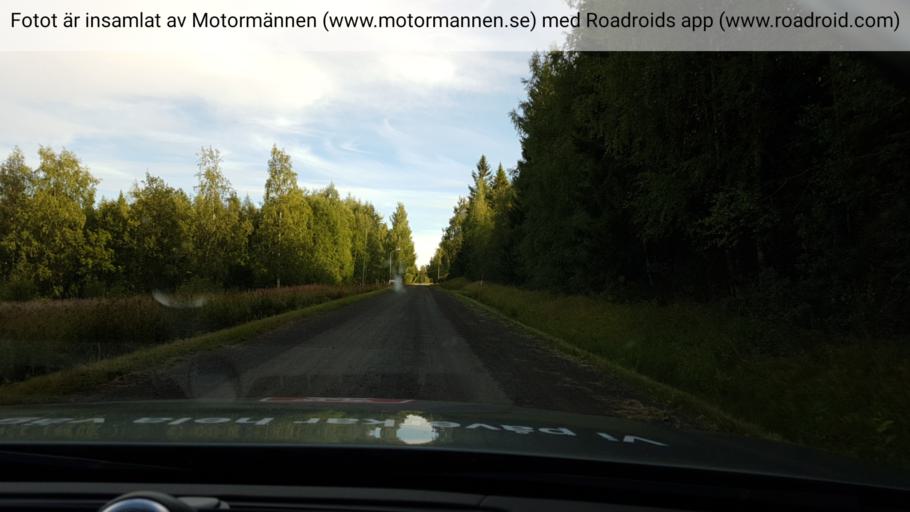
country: SE
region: Jaemtland
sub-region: Stroemsunds Kommun
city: Stroemsund
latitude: 64.1180
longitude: 15.8089
